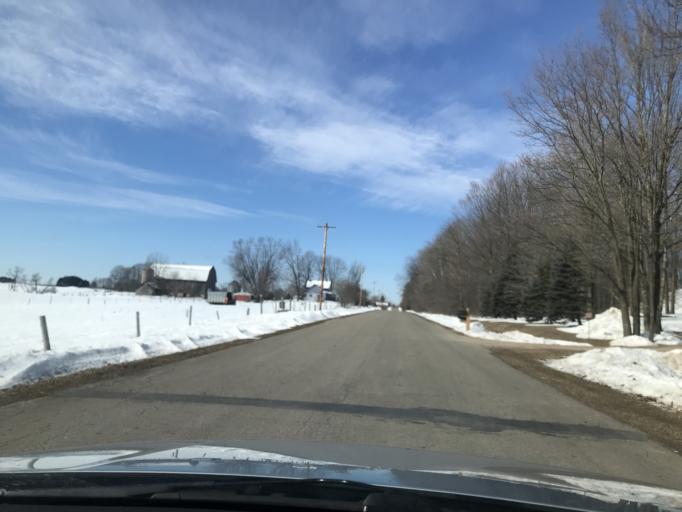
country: US
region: Wisconsin
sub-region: Oconto County
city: Gillett
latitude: 44.9691
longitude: -88.3063
